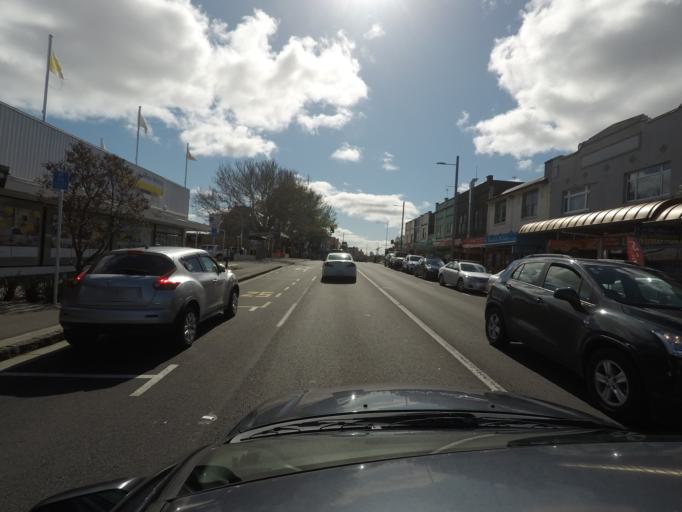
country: NZ
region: Auckland
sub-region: Auckland
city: Rosebank
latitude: -36.8847
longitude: 174.7148
